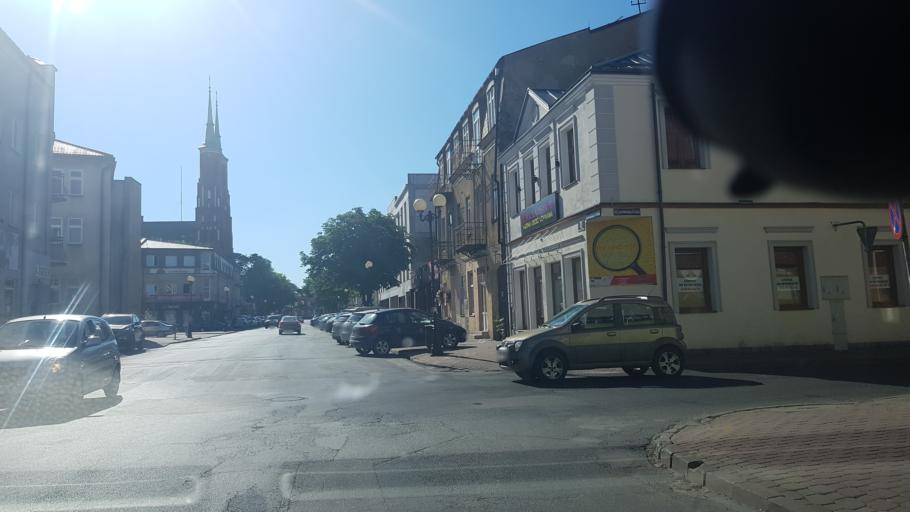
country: PL
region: Masovian Voivodeship
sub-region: Siedlce
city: Siedlce
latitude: 52.1694
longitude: 22.2775
